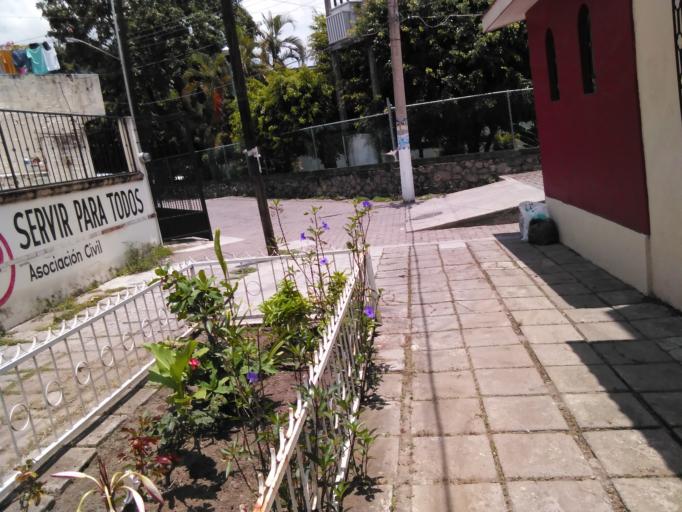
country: MX
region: Nayarit
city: Tepic
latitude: 21.5174
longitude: -104.9164
